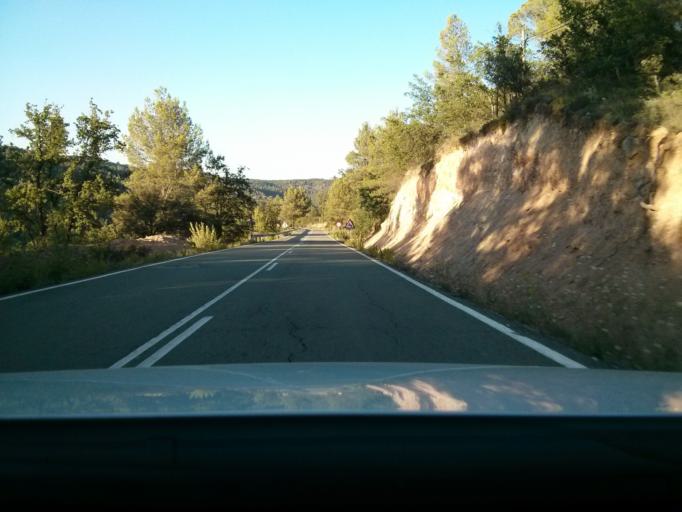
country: ES
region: Castille-La Mancha
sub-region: Provincia de Guadalajara
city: Mantiel
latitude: 40.6251
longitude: -2.6689
